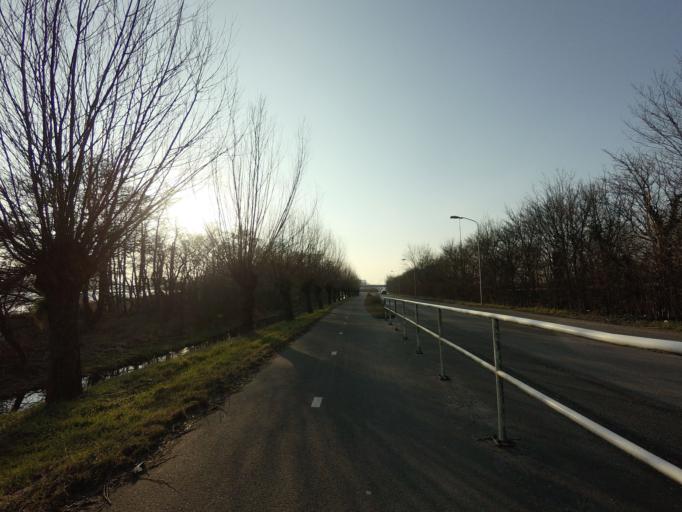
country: NL
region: North Holland
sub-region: Gemeente Haarlem
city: Haarlem
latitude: 52.3832
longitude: 4.6855
